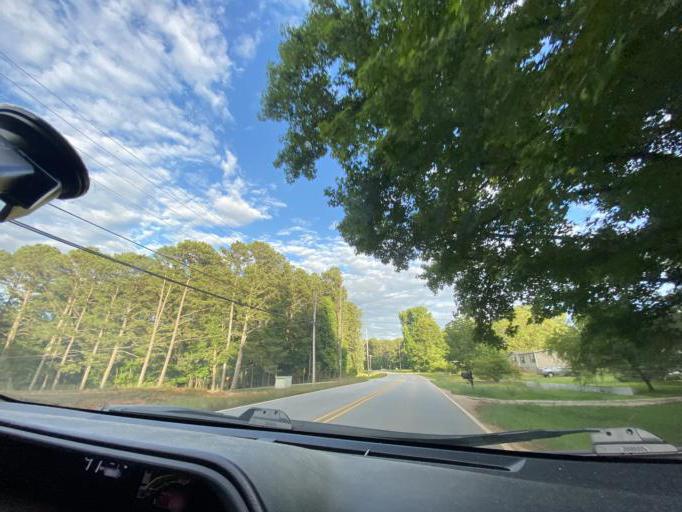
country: US
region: Georgia
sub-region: Fayette County
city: Tyrone
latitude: 33.4338
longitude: -84.6498
